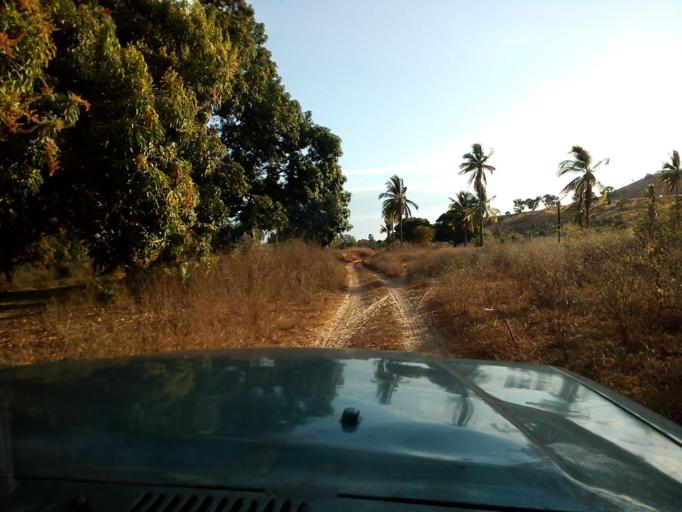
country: MG
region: Boeny
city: Sitampiky
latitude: -16.1255
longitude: 45.5100
